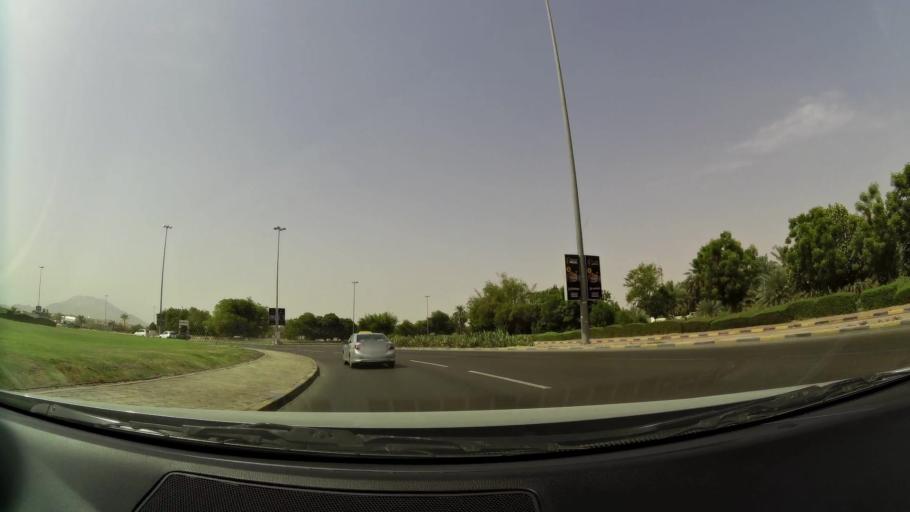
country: AE
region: Abu Dhabi
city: Al Ain
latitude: 24.1684
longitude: 55.7106
